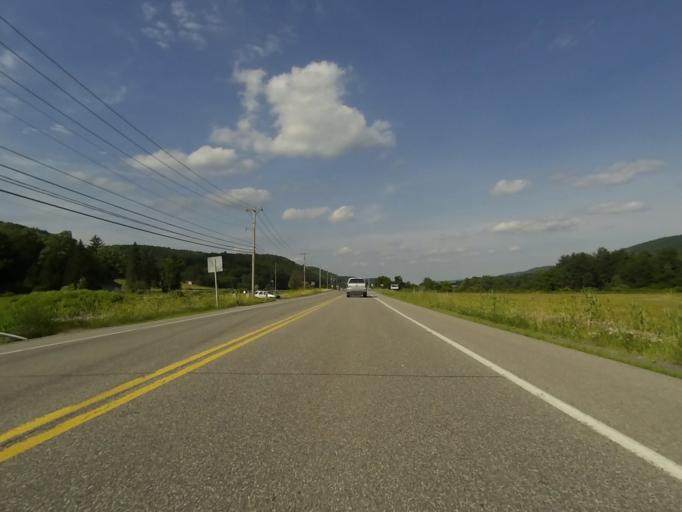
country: US
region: Pennsylvania
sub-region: Centre County
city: Stormstown
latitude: 40.8252
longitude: -78.0239
